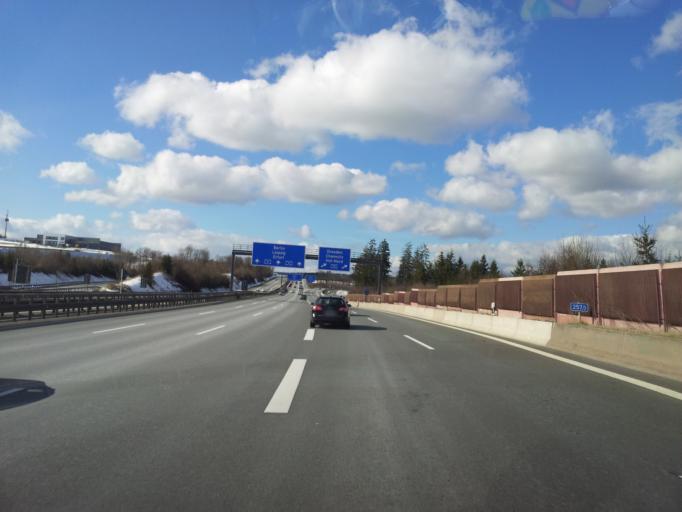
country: DE
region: Bavaria
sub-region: Upper Franconia
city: Leupoldsgrun
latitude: 50.3177
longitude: 11.7980
